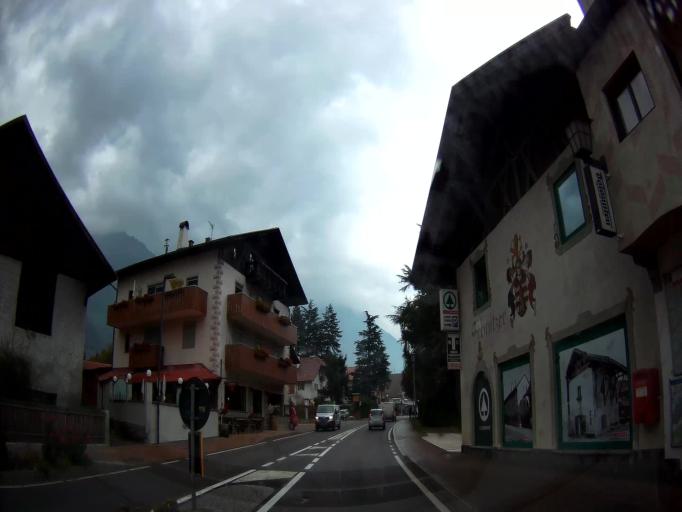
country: IT
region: Trentino-Alto Adige
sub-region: Bolzano
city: Rabla
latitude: 46.6695
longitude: 11.0603
